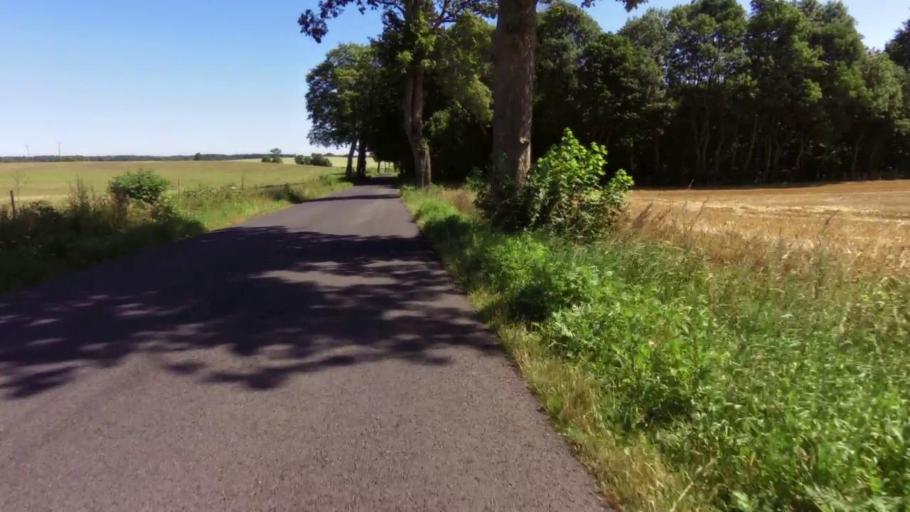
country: PL
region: West Pomeranian Voivodeship
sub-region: Powiat drawski
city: Czaplinek
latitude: 53.5601
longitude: 16.2896
